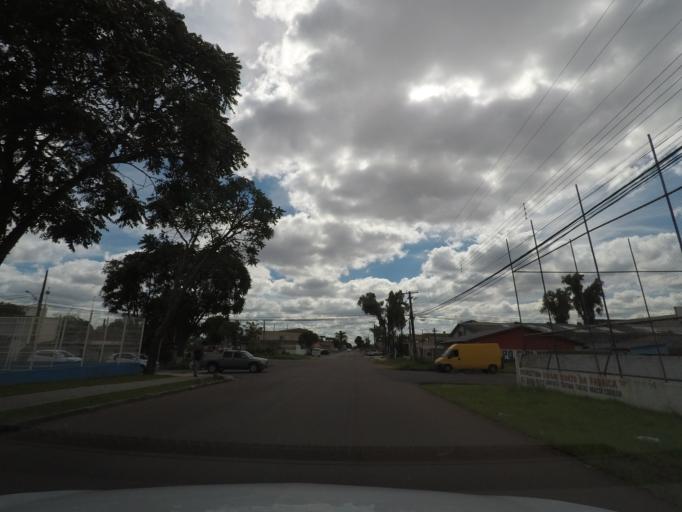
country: BR
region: Parana
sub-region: Sao Jose Dos Pinhais
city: Sao Jose dos Pinhais
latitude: -25.4891
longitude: -49.2396
